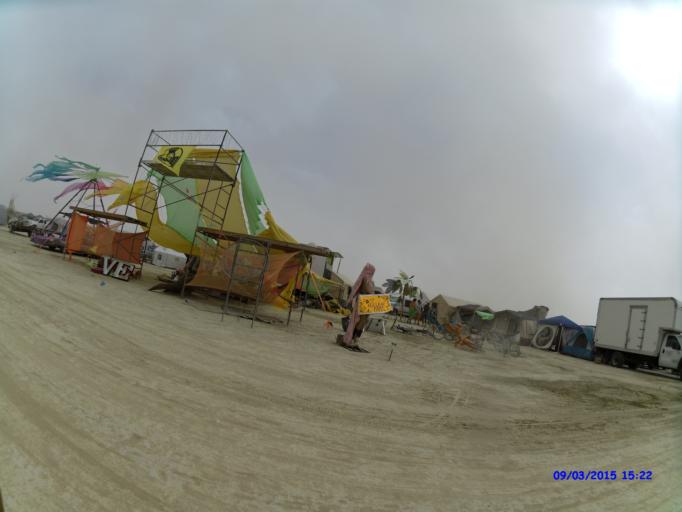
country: US
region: Nevada
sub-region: Pershing County
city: Lovelock
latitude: 40.7778
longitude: -119.2047
